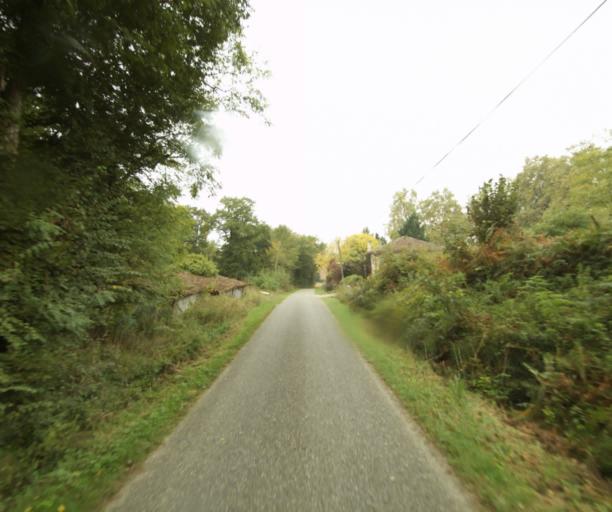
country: FR
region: Midi-Pyrenees
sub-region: Departement du Gers
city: Cazaubon
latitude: 43.9172
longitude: -0.1892
